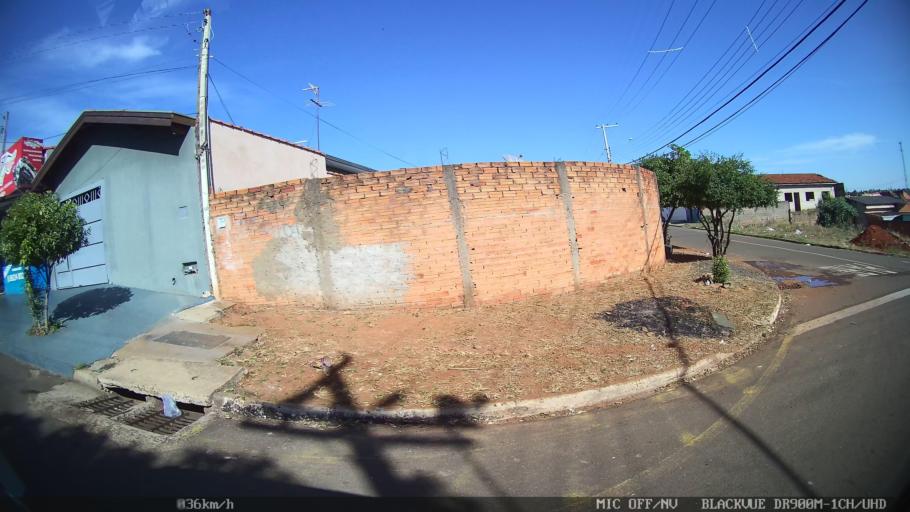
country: BR
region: Sao Paulo
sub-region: Franca
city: Franca
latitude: -20.4901
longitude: -47.4277
